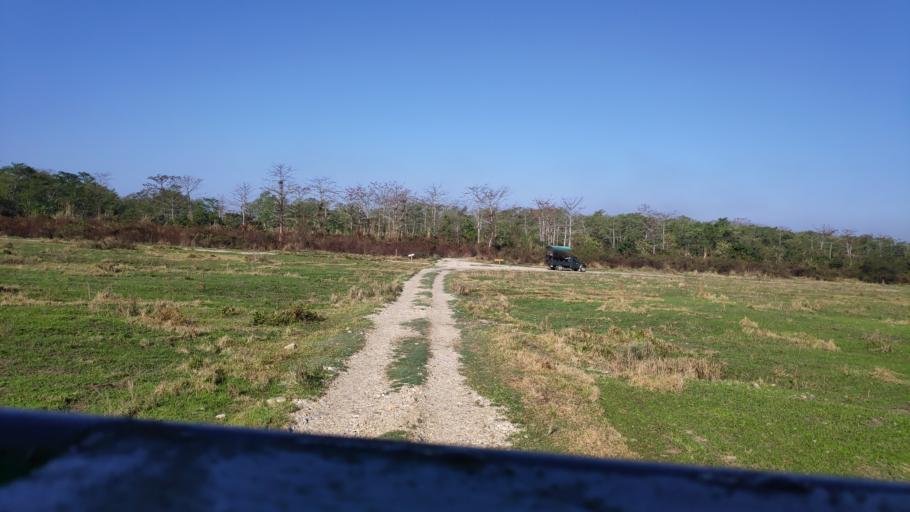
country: NP
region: Central Region
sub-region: Narayani Zone
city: Bharatpur
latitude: 27.5605
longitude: 84.5230
